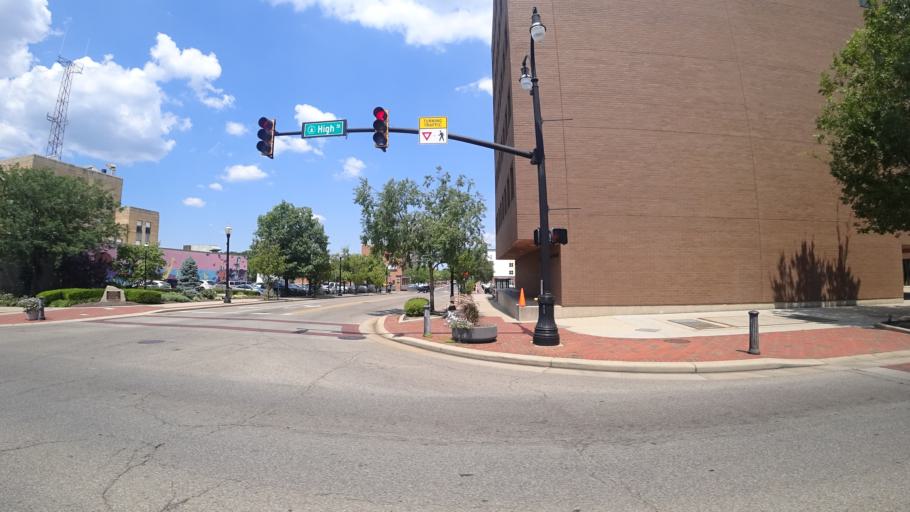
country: US
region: Ohio
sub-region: Butler County
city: Hamilton
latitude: 39.4002
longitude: -84.5633
